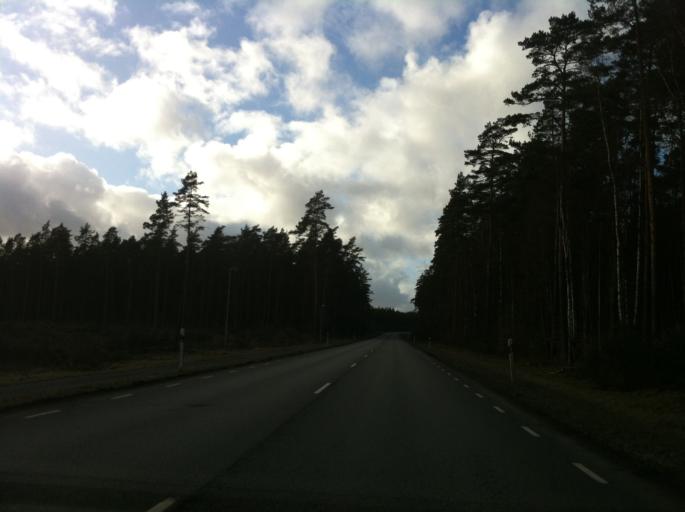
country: SE
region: Skane
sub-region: Bromolla Kommun
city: Bromoella
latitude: 56.0632
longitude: 14.5066
